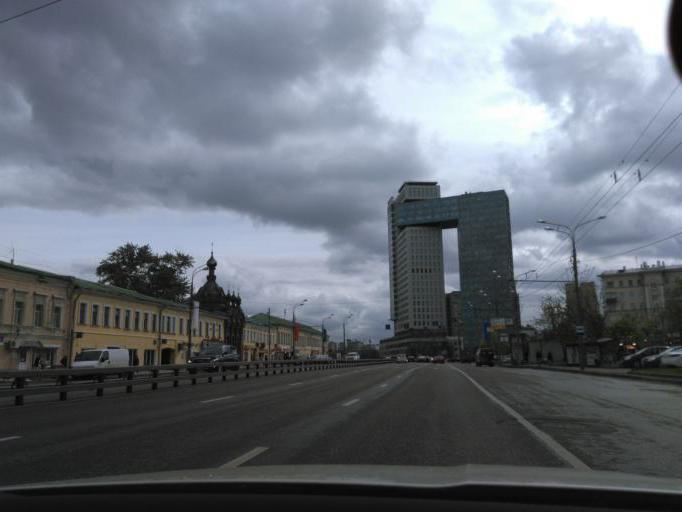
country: RU
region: Moscow
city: Taganskiy
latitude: 55.7468
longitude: 37.6772
